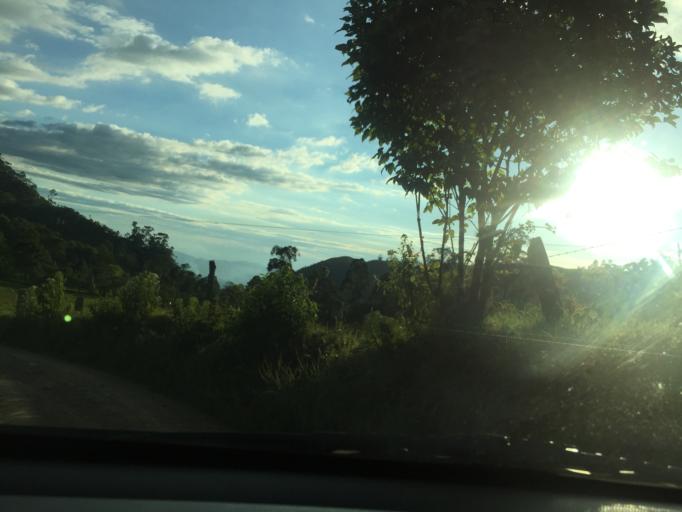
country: CO
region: Cundinamarca
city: Zipacon
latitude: 4.7225
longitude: -74.3898
